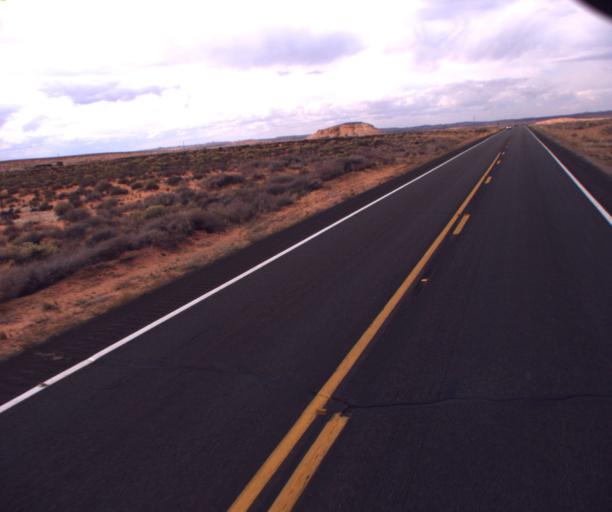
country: US
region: Arizona
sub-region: Apache County
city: Many Farms
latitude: 36.9271
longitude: -109.6183
